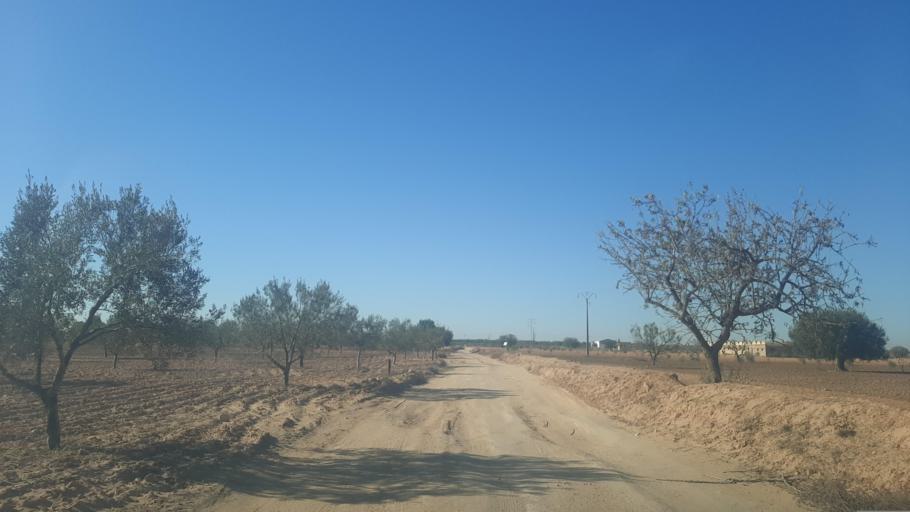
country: TN
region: Safaqis
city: Sfax
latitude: 34.8866
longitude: 10.5861
